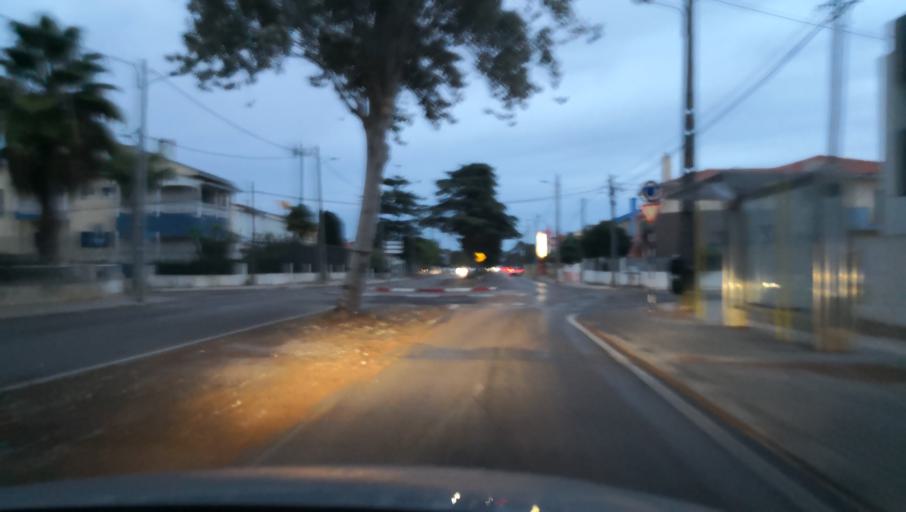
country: PT
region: Setubal
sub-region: Seixal
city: Amora
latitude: 38.6010
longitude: -9.1390
